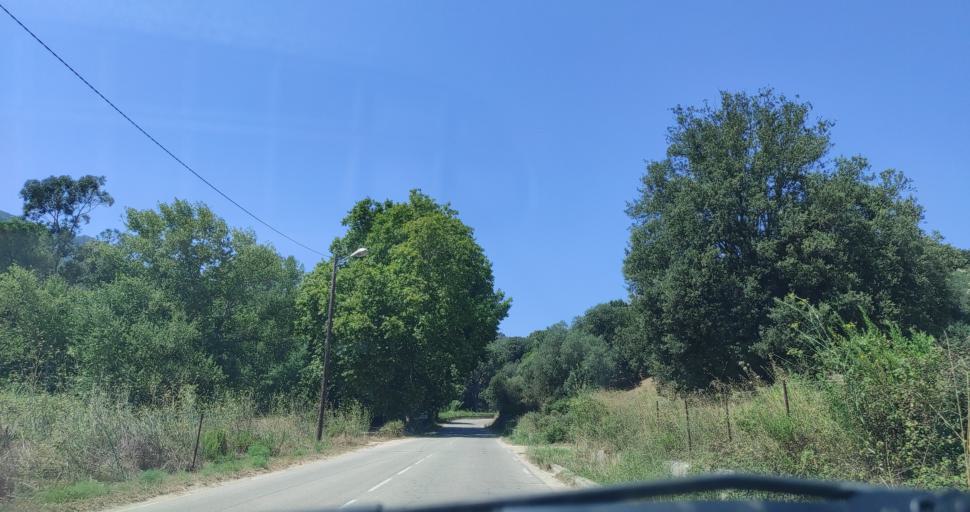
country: FR
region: Corsica
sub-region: Departement de la Corse-du-Sud
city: Ajaccio
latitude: 41.9511
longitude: 8.7334
